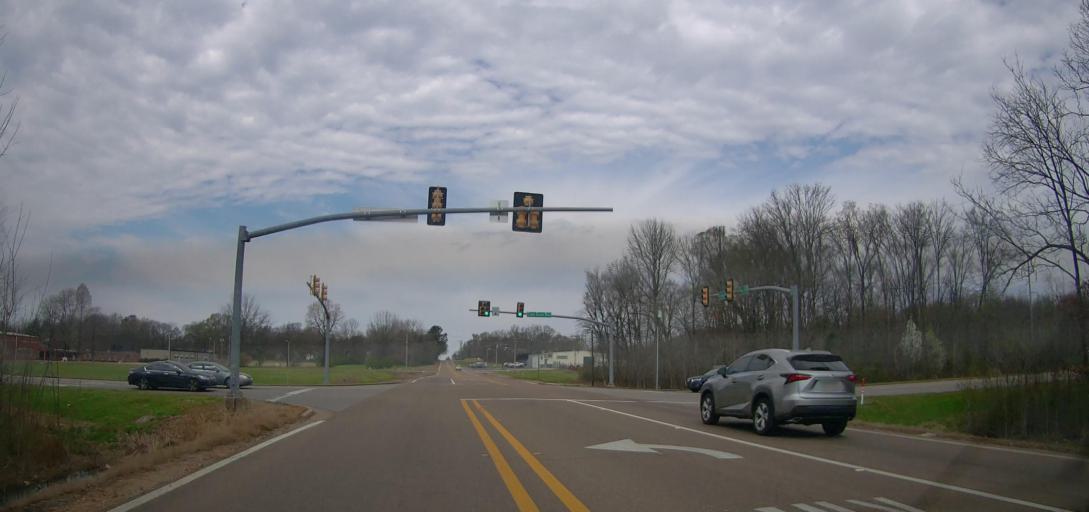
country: US
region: Mississippi
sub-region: De Soto County
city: Olive Branch
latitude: 34.9689
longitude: -89.8353
